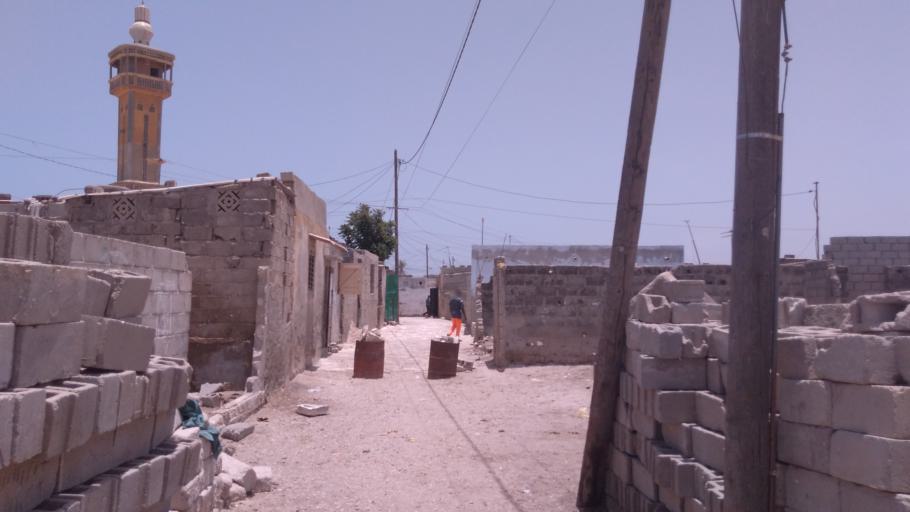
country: SN
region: Dakar
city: Pikine
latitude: 14.6867
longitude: -17.2266
